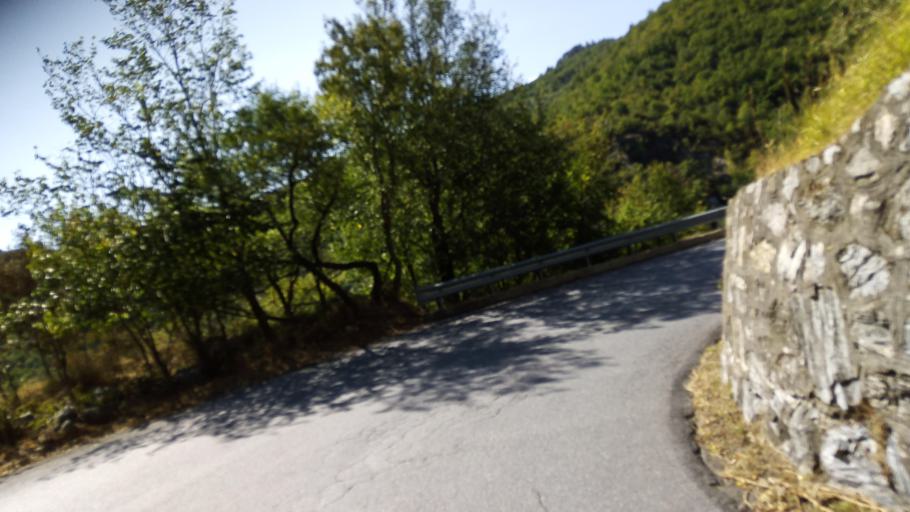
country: IT
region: Liguria
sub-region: Provincia di Savona
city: Balestrino
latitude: 44.1402
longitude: 8.1623
